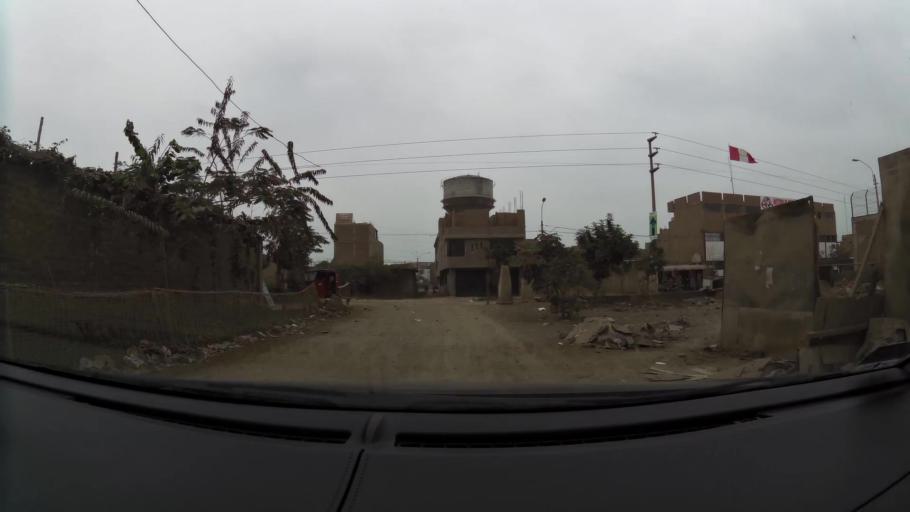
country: PE
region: Lima
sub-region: Lima
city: Independencia
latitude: -11.9540
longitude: -77.0905
